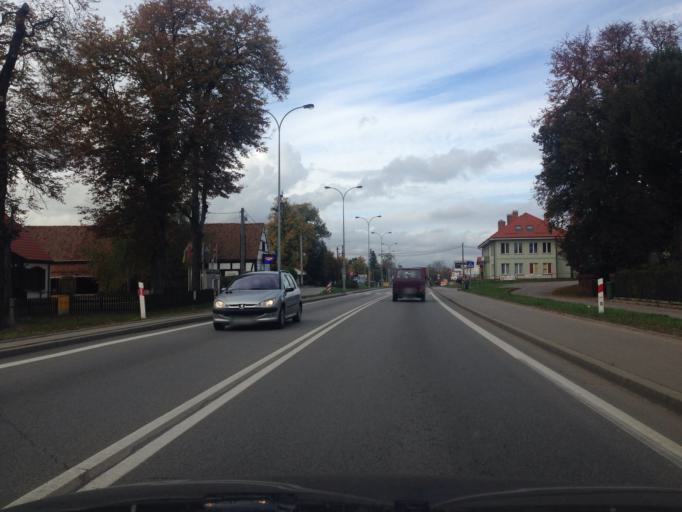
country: PL
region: Pomeranian Voivodeship
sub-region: Powiat gdanski
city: Legowo
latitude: 54.2203
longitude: 18.6480
